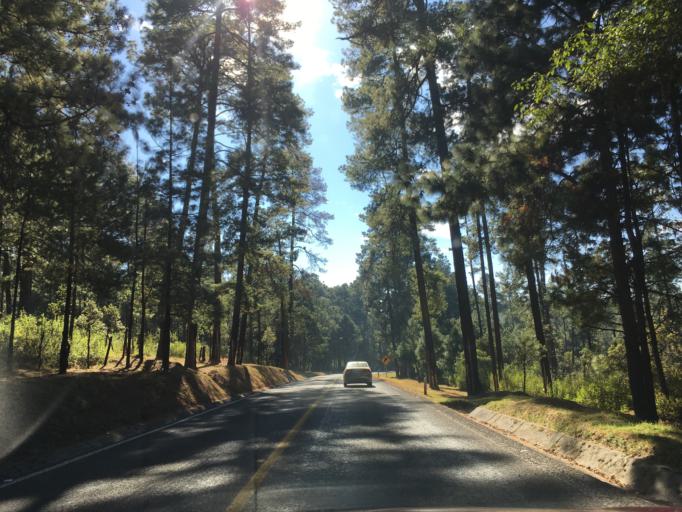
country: MX
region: Michoacan
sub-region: Hidalgo
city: Tierras Coloradas (San Pedro)
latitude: 19.6986
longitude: -100.7427
